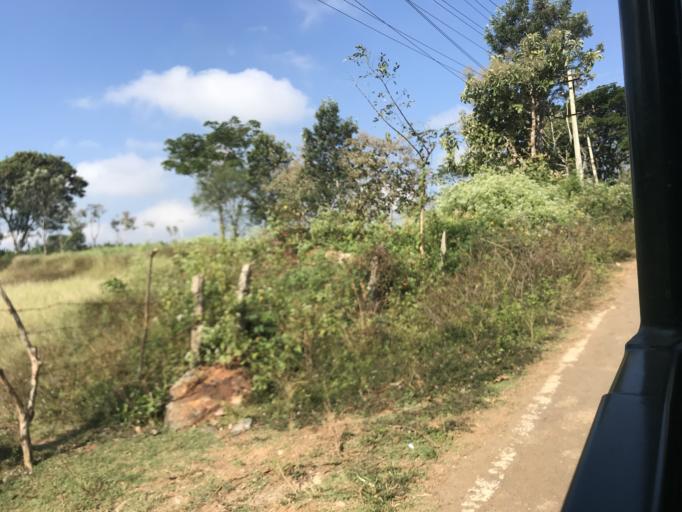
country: IN
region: Karnataka
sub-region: Mysore
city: Sargur
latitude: 11.9426
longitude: 76.2683
